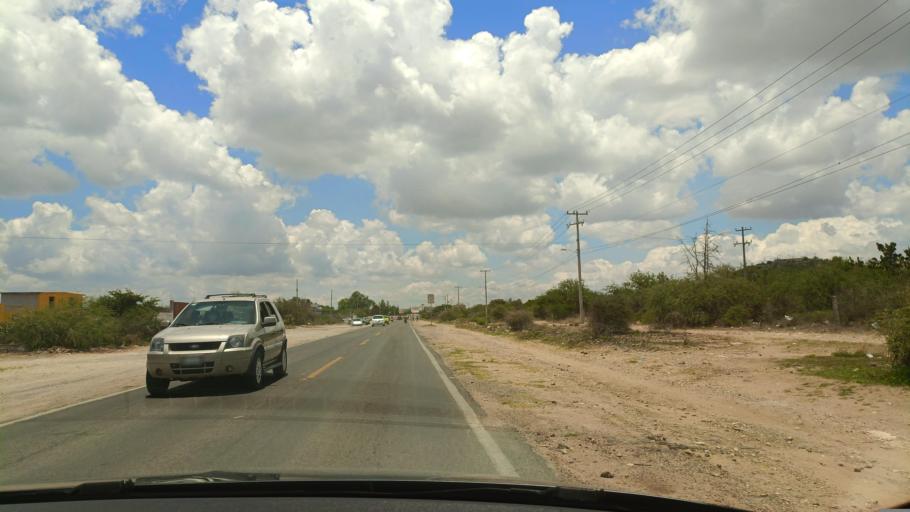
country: MX
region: Guerrero
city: San Luis de la Paz
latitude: 21.2861
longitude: -100.5069
